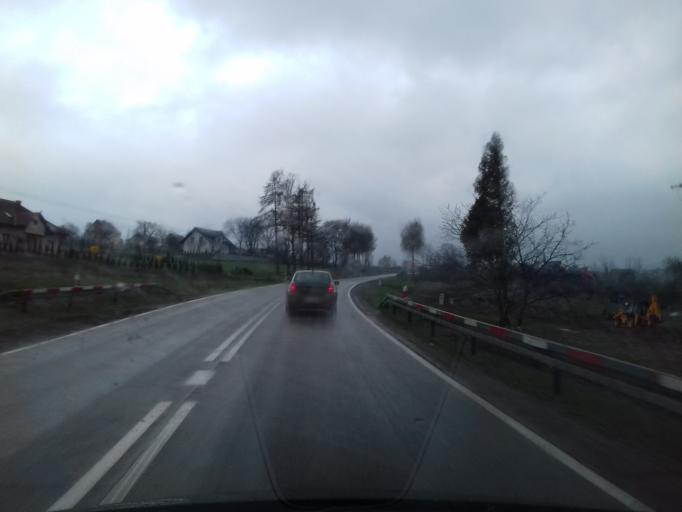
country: PL
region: Lesser Poland Voivodeship
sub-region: Powiat nowosadecki
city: Chelmiec
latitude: 49.6346
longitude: 20.6282
